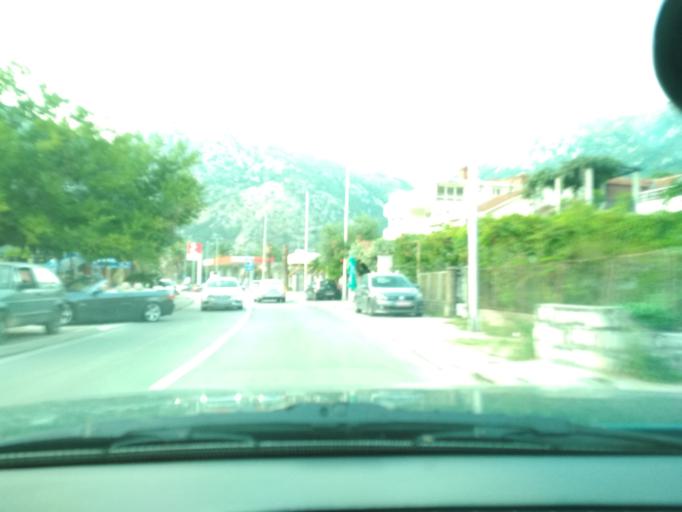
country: ME
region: Kotor
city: Risan
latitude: 42.5100
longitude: 18.6966
